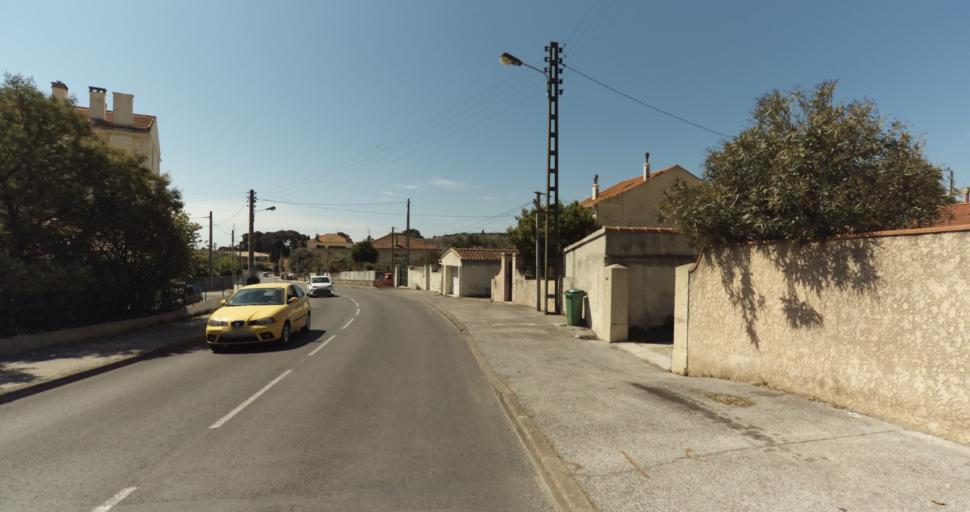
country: FR
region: Provence-Alpes-Cote d'Azur
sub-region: Departement du Var
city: Le Revest-les-Eaux
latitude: 43.1435
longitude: 5.9016
